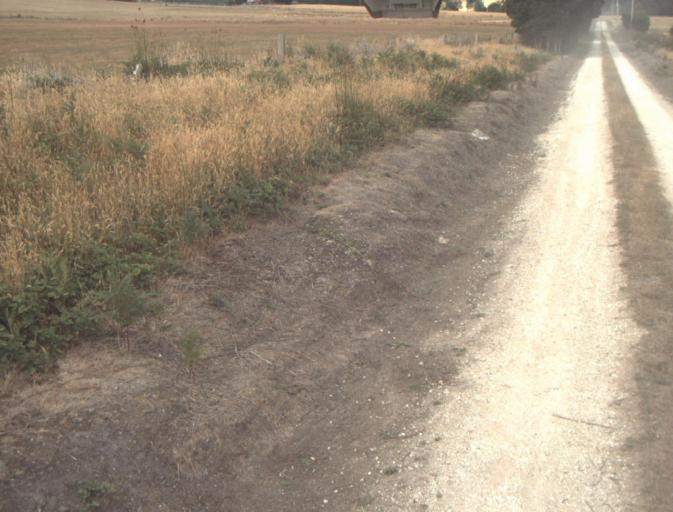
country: AU
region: Tasmania
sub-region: Launceston
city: Mayfield
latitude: -41.1891
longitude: 147.1677
